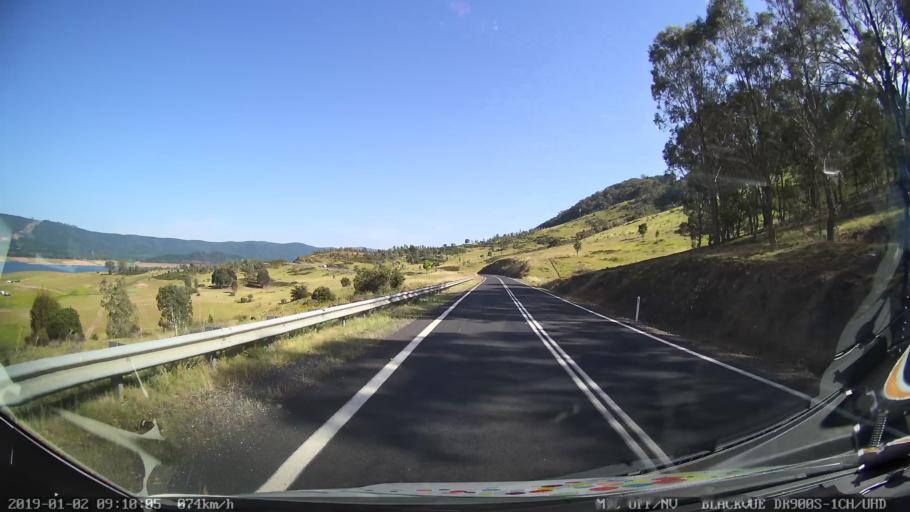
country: AU
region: New South Wales
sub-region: Tumut Shire
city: Tumut
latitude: -35.5248
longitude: 148.2723
